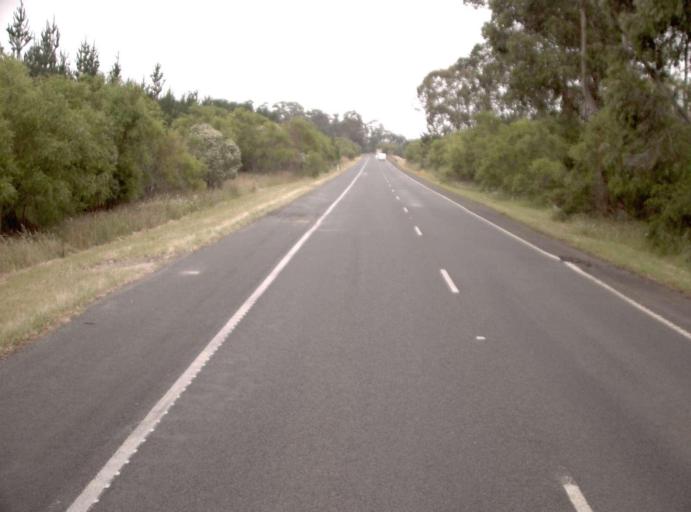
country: AU
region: Victoria
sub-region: Latrobe
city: Morwell
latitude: -38.2916
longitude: 146.2967
